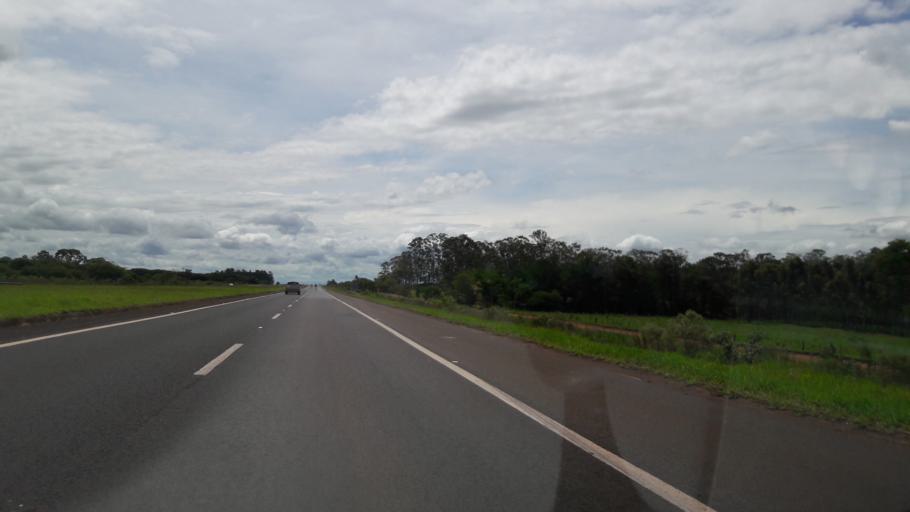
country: BR
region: Sao Paulo
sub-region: Avare
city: Avare
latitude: -22.9338
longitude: -48.9931
